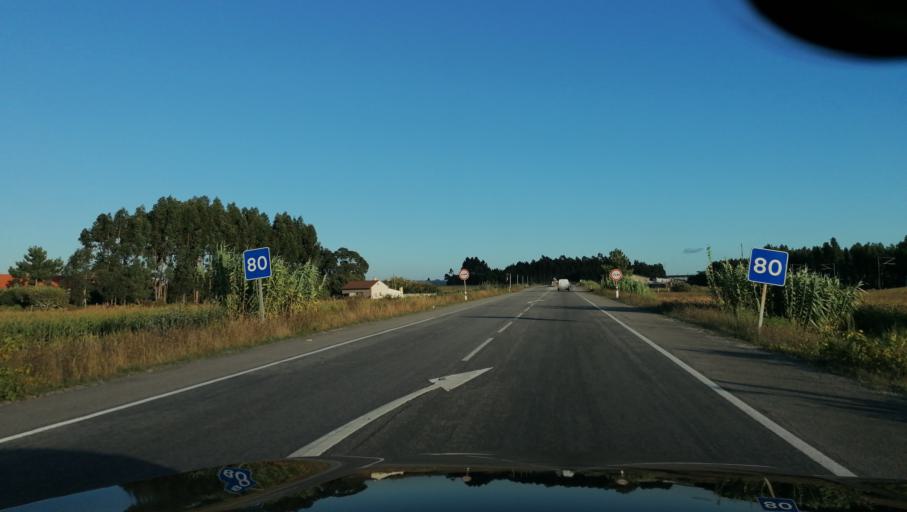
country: PT
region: Aveiro
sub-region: Aveiro
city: Oliveirinha
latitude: 40.6022
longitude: -8.6187
